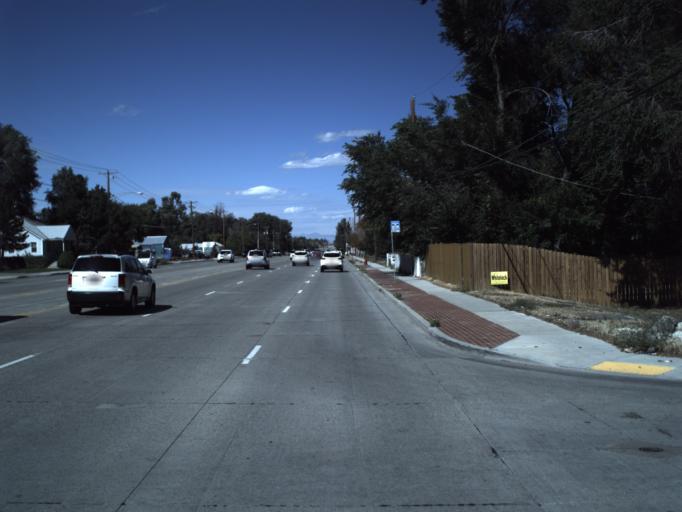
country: US
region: Utah
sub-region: Salt Lake County
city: West Jordan
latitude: 40.5923
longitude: -111.9386
